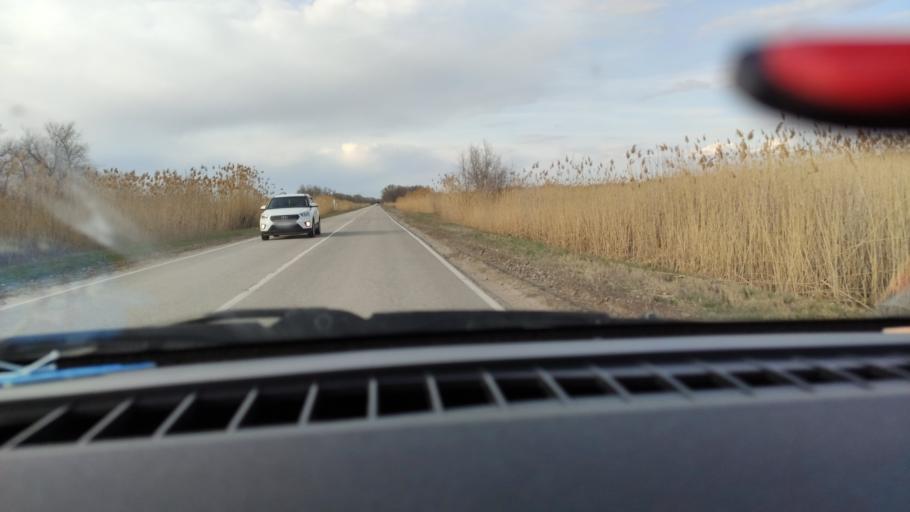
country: RU
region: Saratov
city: Privolzhskiy
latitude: 51.2662
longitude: 45.9463
